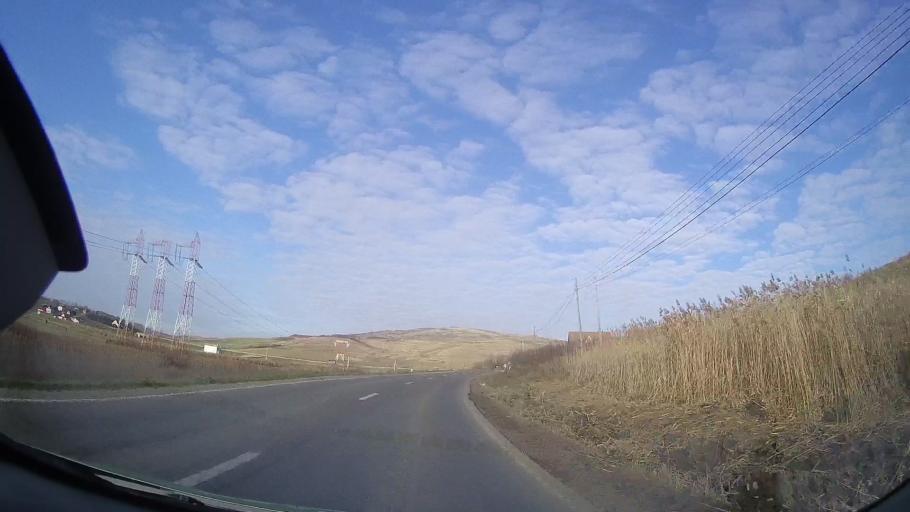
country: RO
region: Cluj
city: Caianu Mic
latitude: 46.8093
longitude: 23.8726
